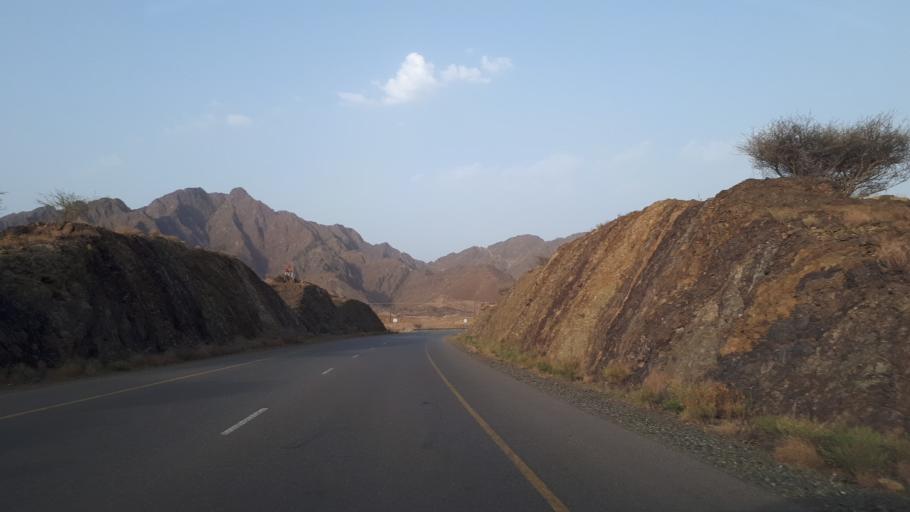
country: OM
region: Al Batinah
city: Rustaq
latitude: 23.4318
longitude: 57.1561
